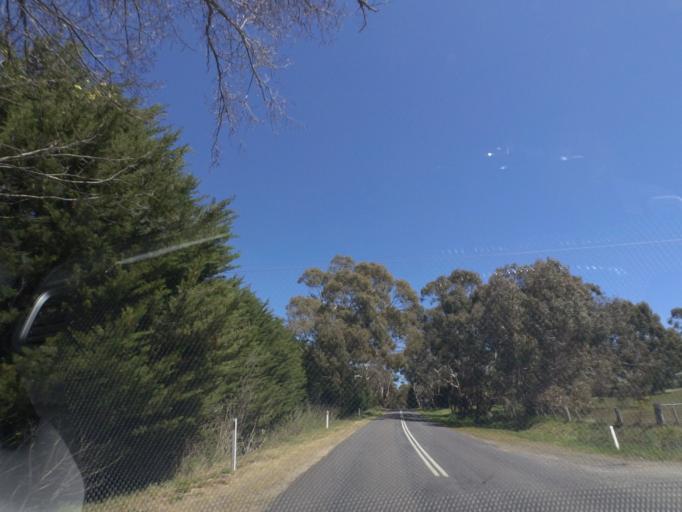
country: AU
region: Victoria
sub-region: Hume
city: Sunbury
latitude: -37.3139
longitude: 144.6742
